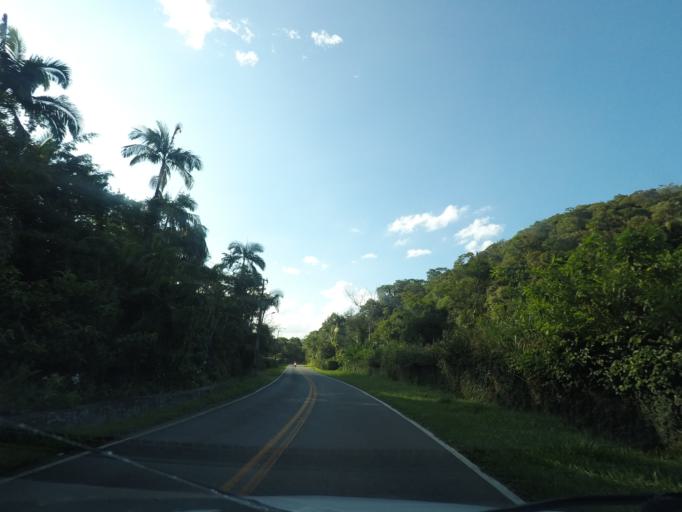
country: BR
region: Parana
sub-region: Antonina
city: Antonina
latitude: -25.4259
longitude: -48.8765
